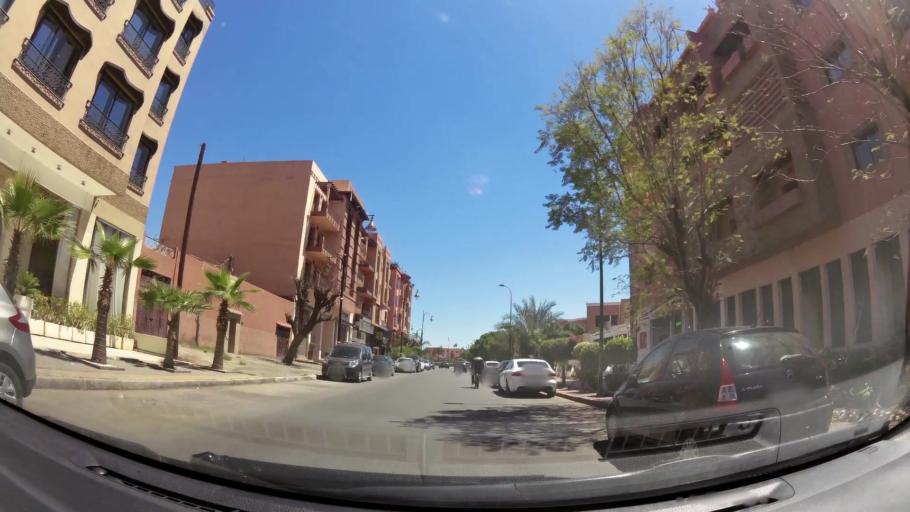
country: MA
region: Marrakech-Tensift-Al Haouz
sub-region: Marrakech
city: Marrakesh
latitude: 31.6269
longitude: -8.0163
